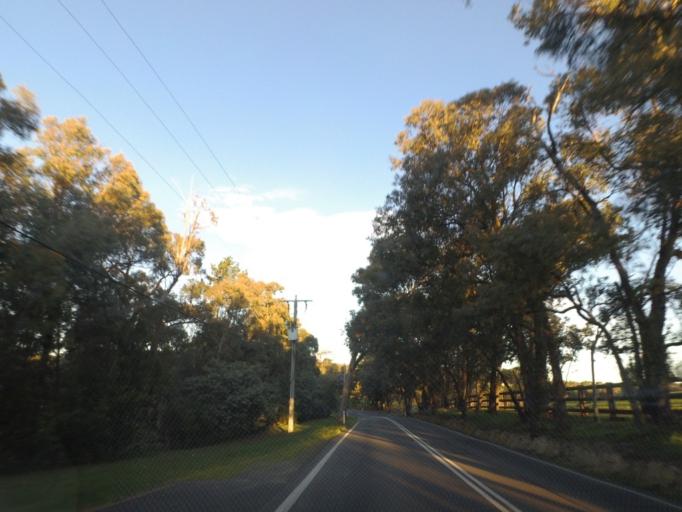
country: AU
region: Victoria
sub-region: Manningham
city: Warrandyte
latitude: -37.7373
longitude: 145.2515
